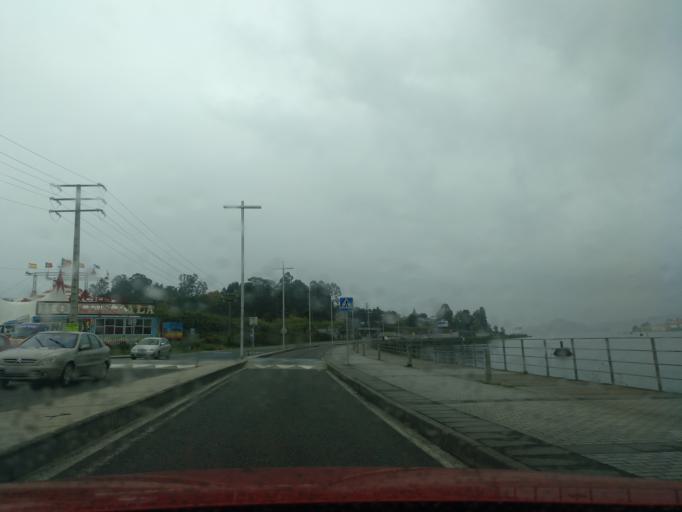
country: ES
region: Galicia
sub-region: Provincia de Pontevedra
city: Poio
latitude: 42.4237
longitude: -8.6557
